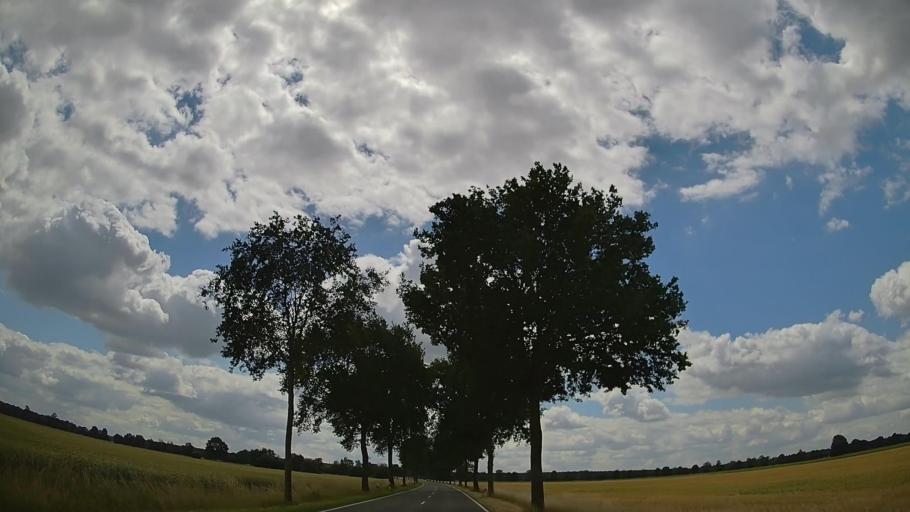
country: DE
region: Lower Saxony
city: Brockum
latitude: 52.4344
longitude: 8.5035
